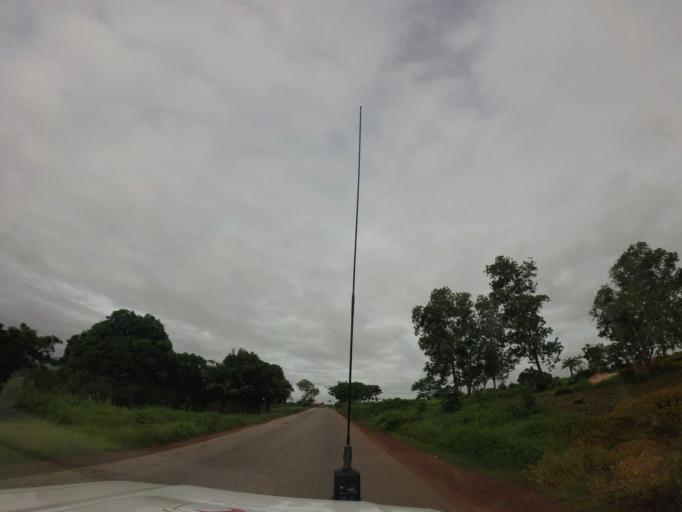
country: GN
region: Kindia
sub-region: Kindia
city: Kindia
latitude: 9.9731
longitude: -12.9275
